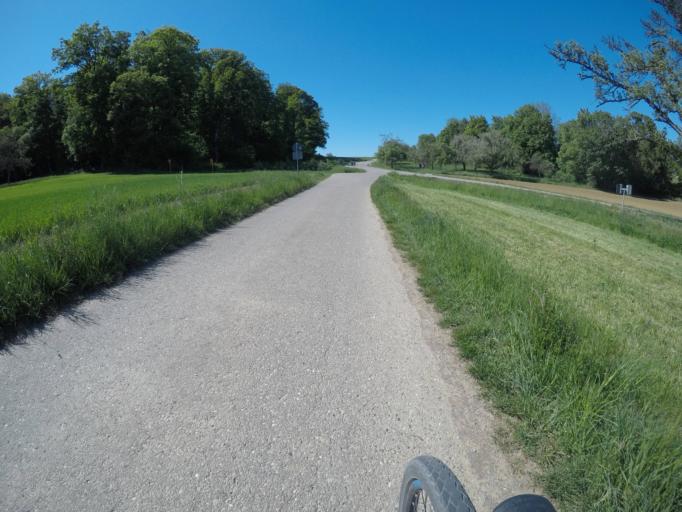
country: DE
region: Baden-Wuerttemberg
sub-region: Regierungsbezirk Stuttgart
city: Weissach
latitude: 48.8382
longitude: 8.8970
